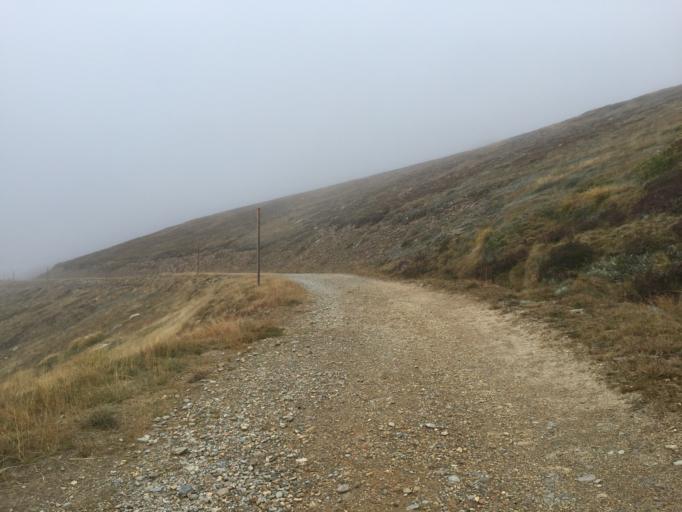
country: AU
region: New South Wales
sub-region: Snowy River
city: Jindabyne
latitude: -36.4553
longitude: 148.2726
